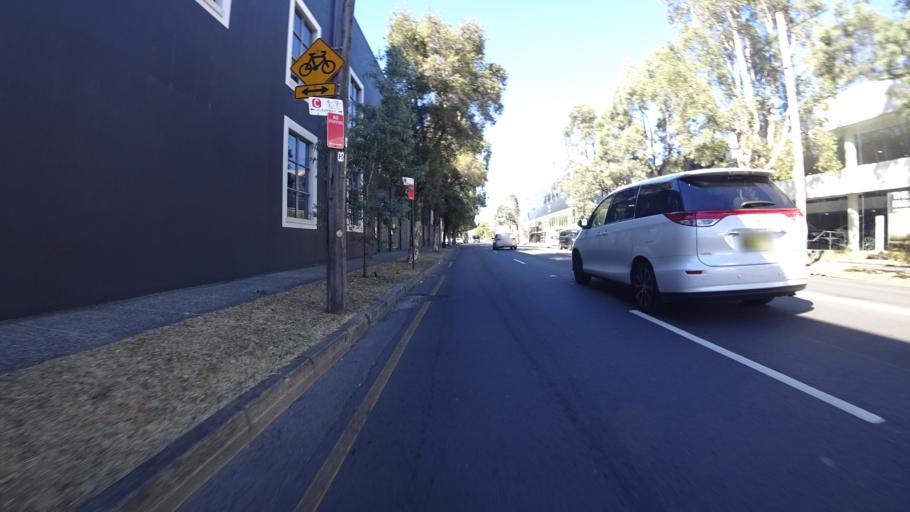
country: AU
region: New South Wales
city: Alexandria
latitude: -33.9158
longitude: 151.1950
